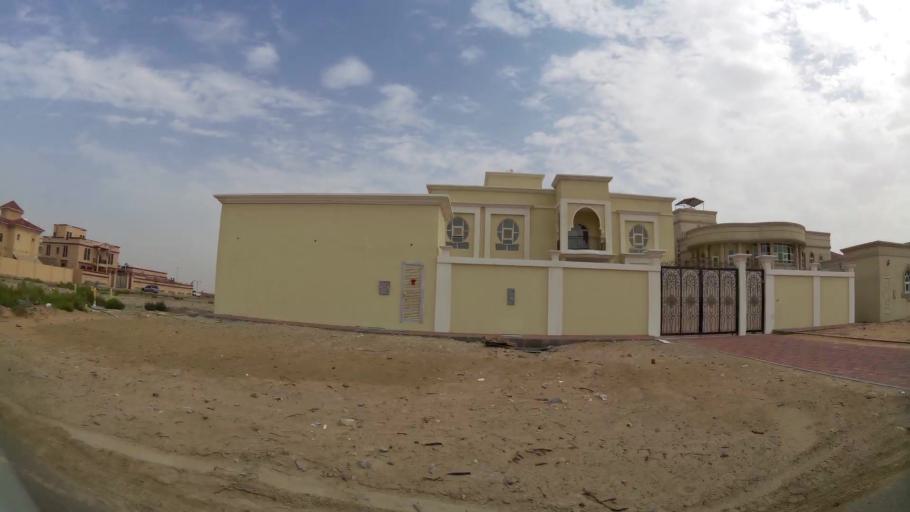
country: AE
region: Abu Dhabi
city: Abu Dhabi
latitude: 24.3113
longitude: 54.6548
